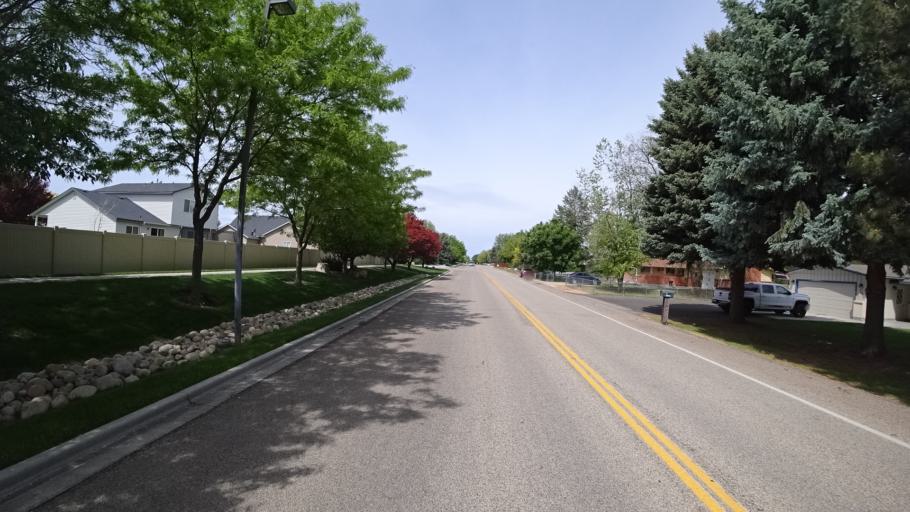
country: US
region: Idaho
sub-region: Ada County
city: Meridian
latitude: 43.5539
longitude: -116.3169
